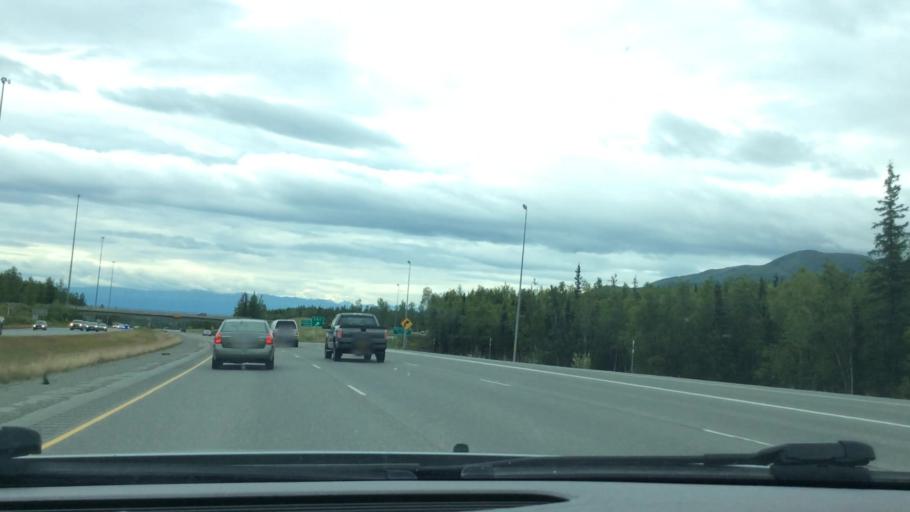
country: US
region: Alaska
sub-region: Anchorage Municipality
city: Eagle River
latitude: 61.2924
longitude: -149.5899
